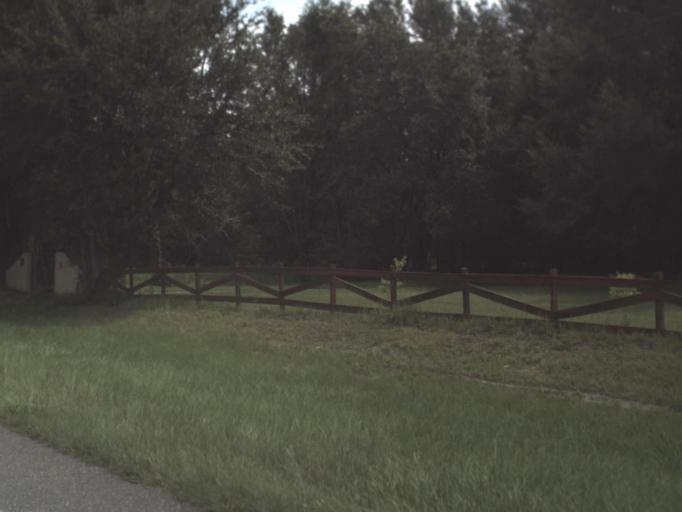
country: US
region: Florida
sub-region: Columbia County
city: Watertown
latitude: 30.0635
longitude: -82.5998
